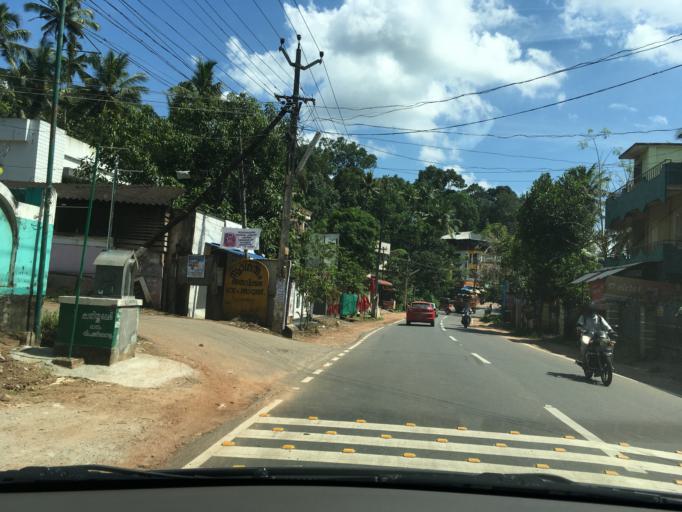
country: IN
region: Kerala
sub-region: Thiruvananthapuram
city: Nedumangad
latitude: 8.5823
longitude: 76.9948
